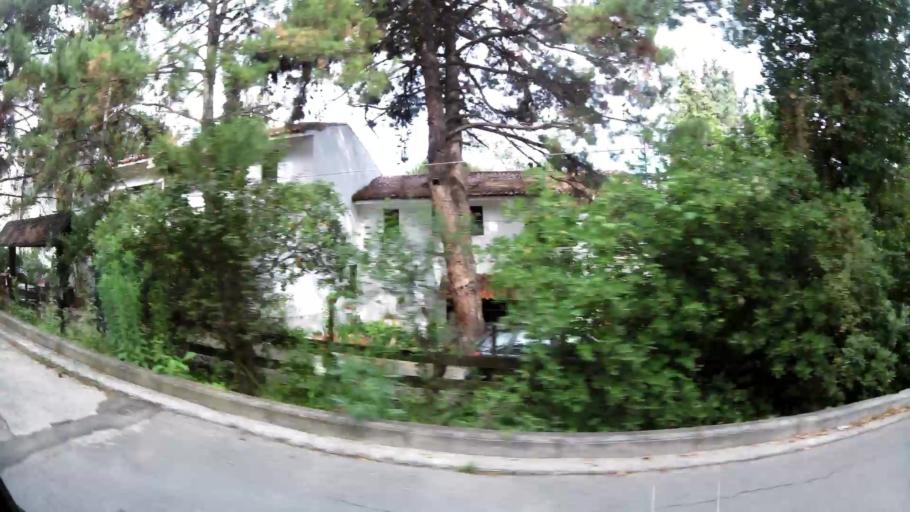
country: GR
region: Central Macedonia
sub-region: Nomos Thessalonikis
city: Panorama
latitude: 40.5890
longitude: 23.0262
